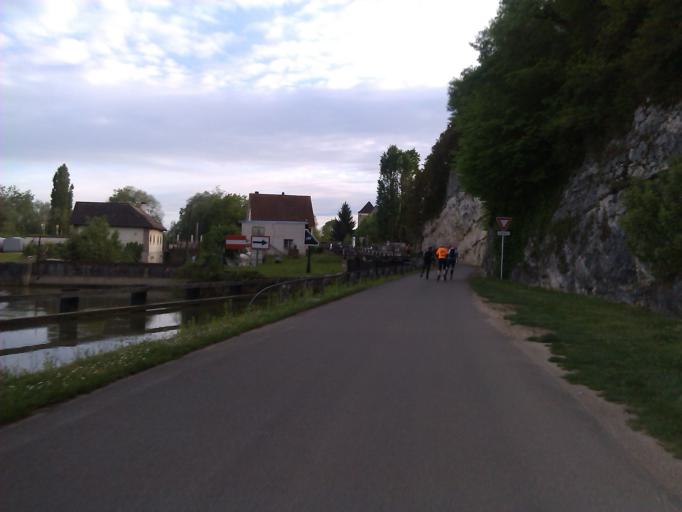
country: FR
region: Franche-Comte
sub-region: Departement du Jura
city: Dole
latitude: 47.1257
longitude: 5.5640
